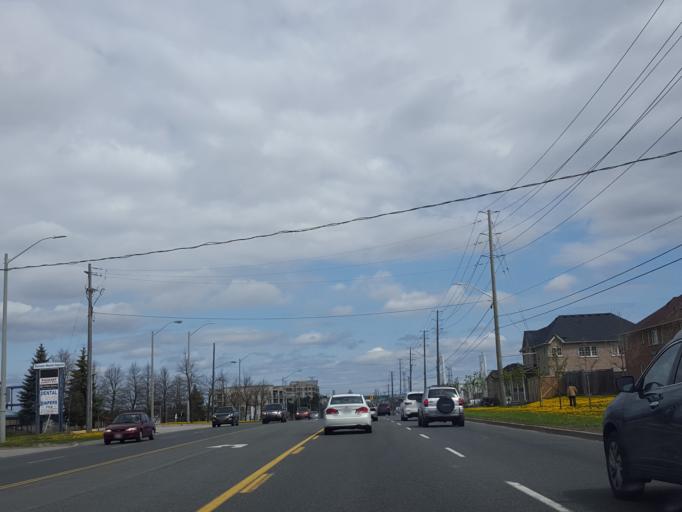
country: CA
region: Ontario
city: Markham
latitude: 43.8425
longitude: -79.2523
